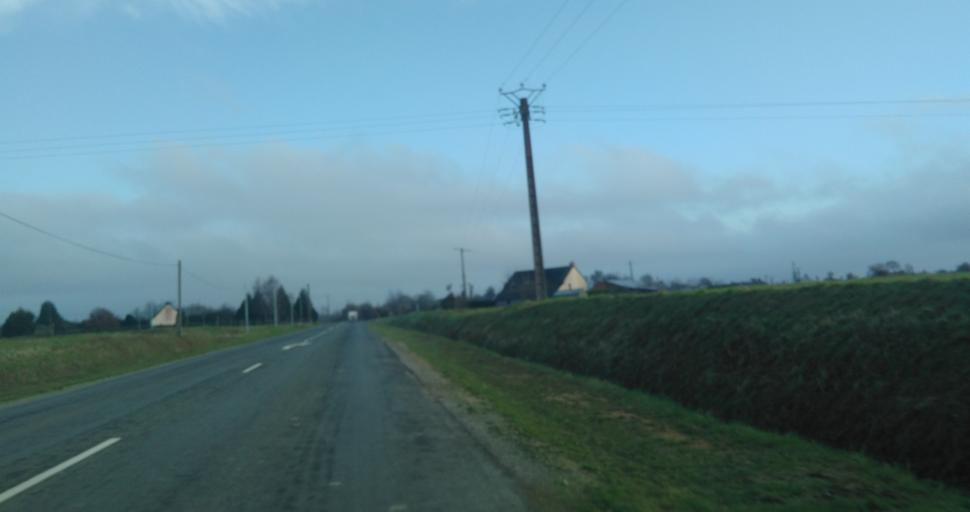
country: FR
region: Brittany
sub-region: Departement d'Ille-et-Vilaine
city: Boisgervilly
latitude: 48.1710
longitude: -2.1110
